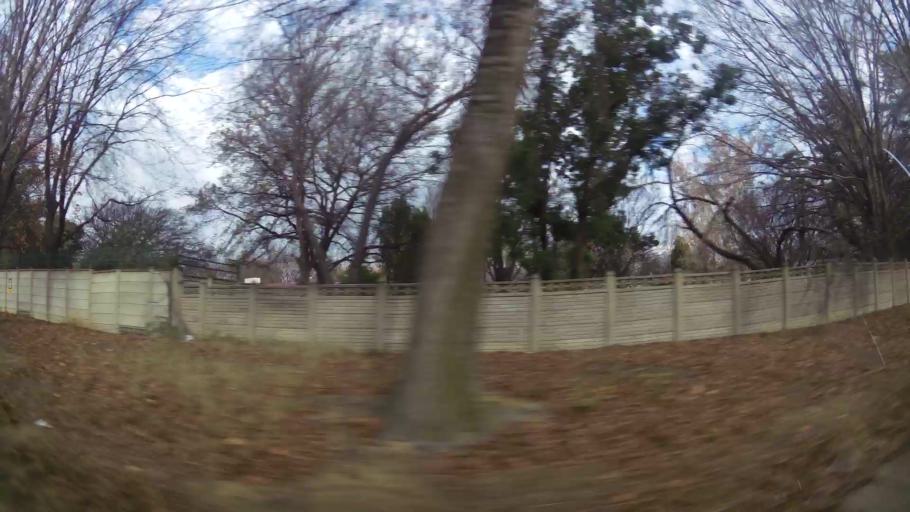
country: ZA
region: Orange Free State
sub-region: Fezile Dabi District Municipality
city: Sasolburg
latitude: -26.7975
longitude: 27.8222
